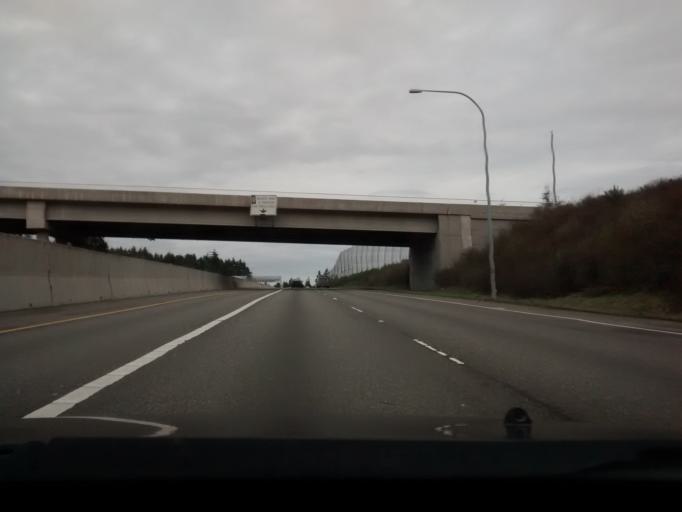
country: US
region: Washington
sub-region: Pierce County
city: Wollochet
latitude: 47.2792
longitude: -122.5606
